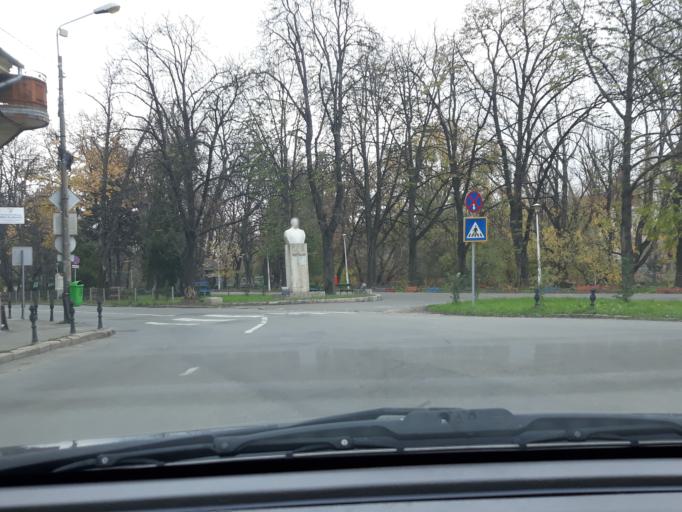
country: RO
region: Bihor
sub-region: Comuna Biharea
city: Oradea
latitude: 47.0559
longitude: 21.9334
